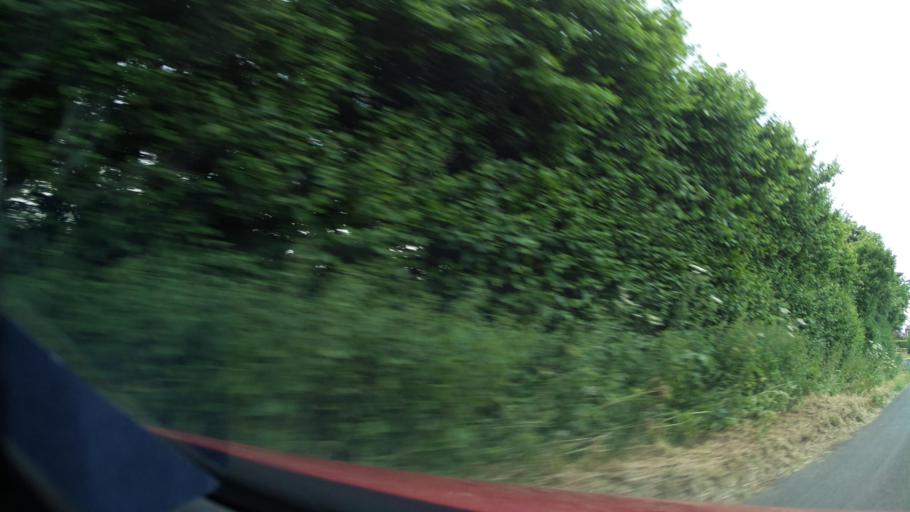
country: GB
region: England
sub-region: Somerset
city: Yeovil
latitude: 50.9233
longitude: -2.5881
